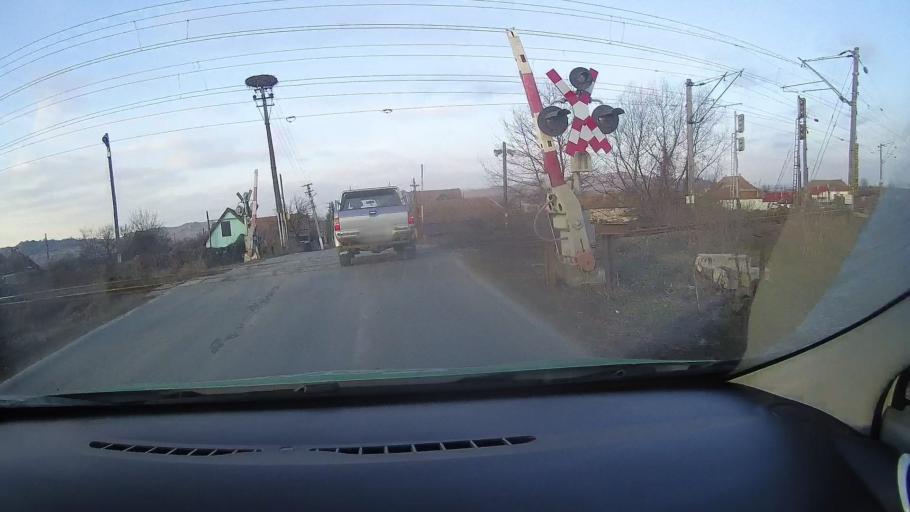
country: RO
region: Mures
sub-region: Comuna Vanatori
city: Vanatori
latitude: 46.2431
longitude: 24.9231
